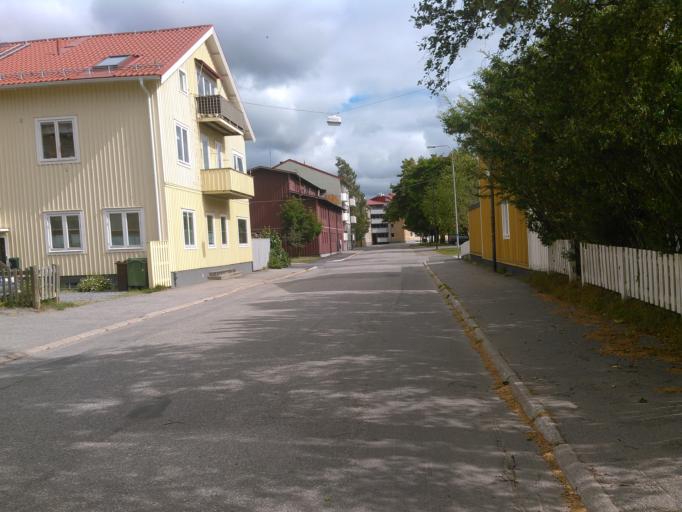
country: SE
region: Vaesterbotten
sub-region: Umea Kommun
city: Umea
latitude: 63.8289
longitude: 20.2467
